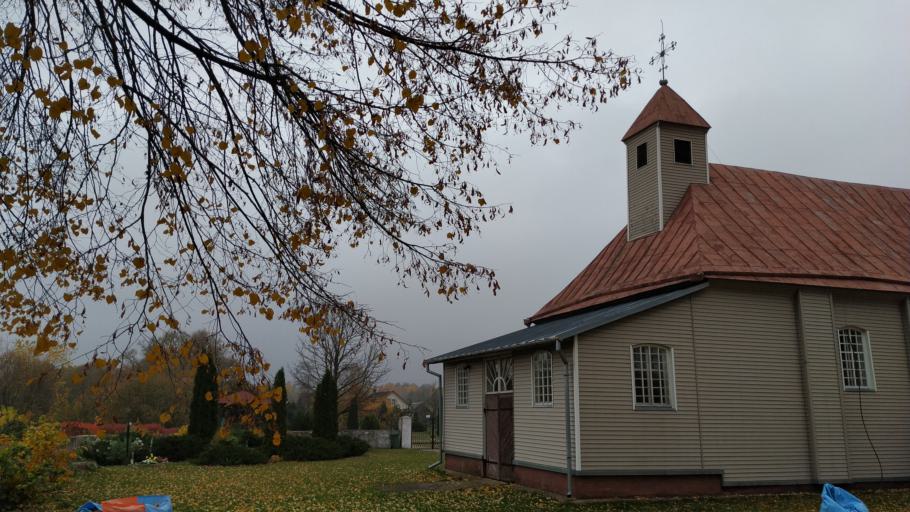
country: LT
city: Skaidiskes
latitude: 54.6478
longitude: 25.6225
